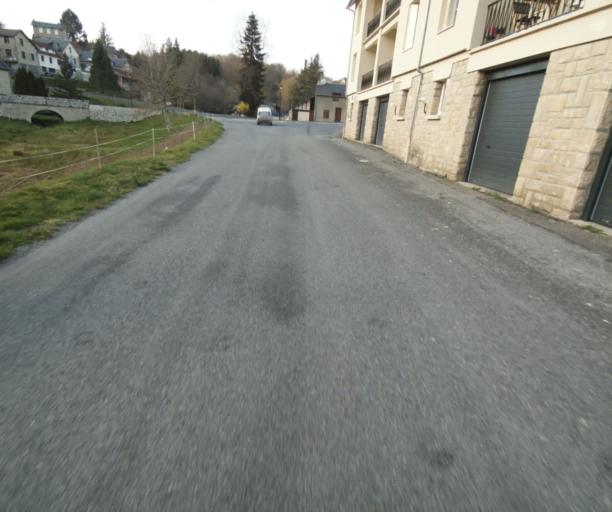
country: FR
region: Limousin
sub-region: Departement de la Correze
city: Correze
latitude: 45.3729
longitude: 1.8773
